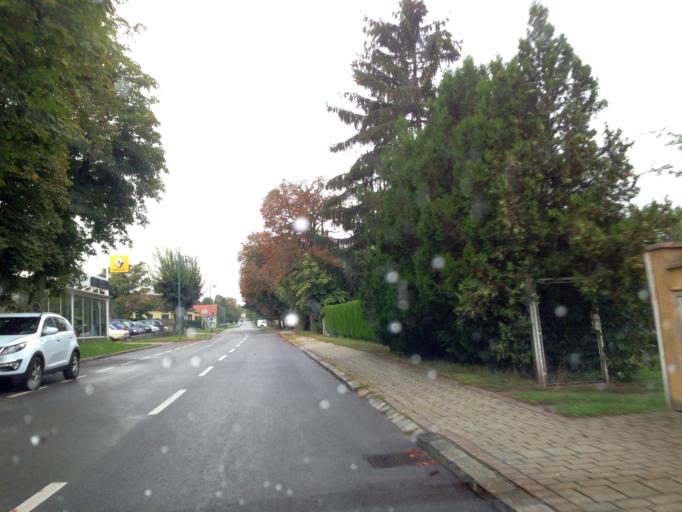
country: AT
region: Burgenland
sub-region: Politischer Bezirk Neusiedl am See
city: Potzneusiedl
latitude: 48.0435
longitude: 16.9488
